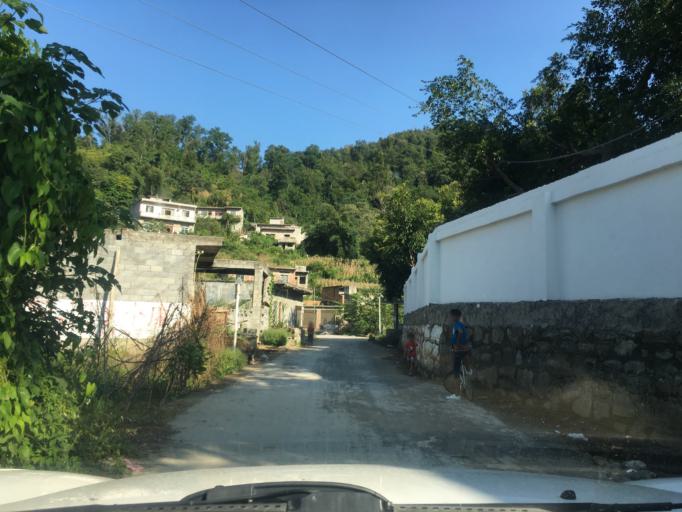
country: CN
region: Guangxi Zhuangzu Zizhiqu
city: Xinzhou
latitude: 25.4413
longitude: 105.7387
